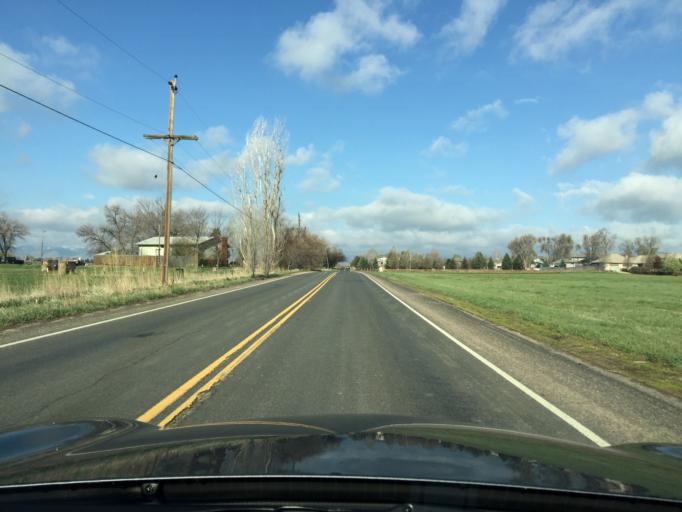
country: US
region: Colorado
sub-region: Boulder County
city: Longmont
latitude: 40.1307
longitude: -105.1126
